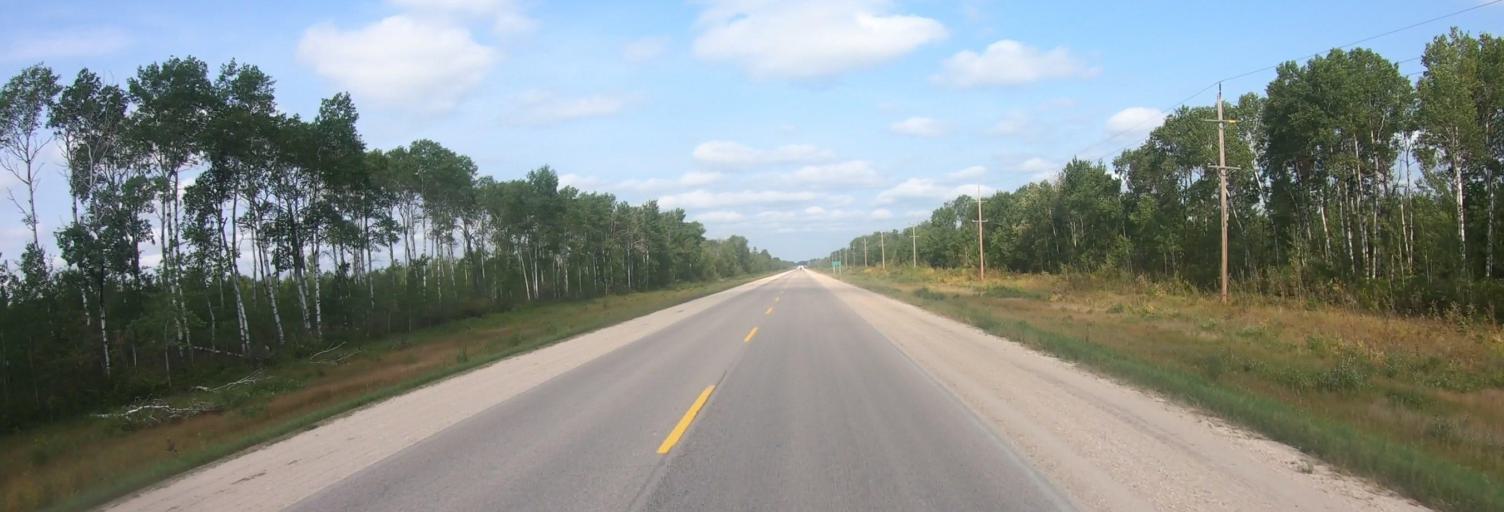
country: CA
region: Manitoba
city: La Broquerie
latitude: 49.1975
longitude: -96.2670
